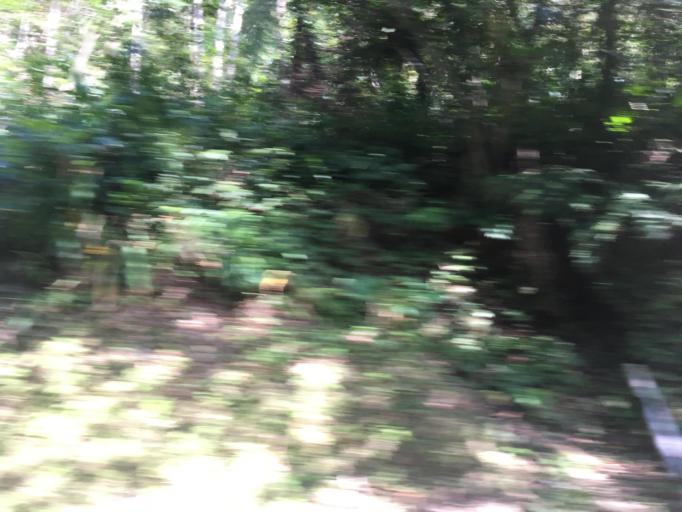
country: TW
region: Taiwan
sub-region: Yilan
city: Yilan
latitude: 24.7557
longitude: 121.6230
